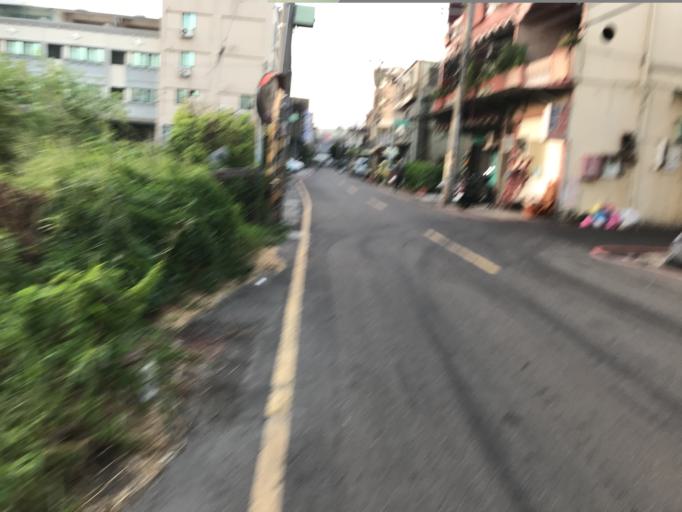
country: TW
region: Taiwan
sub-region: Hsinchu
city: Hsinchu
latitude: 24.8042
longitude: 120.9386
